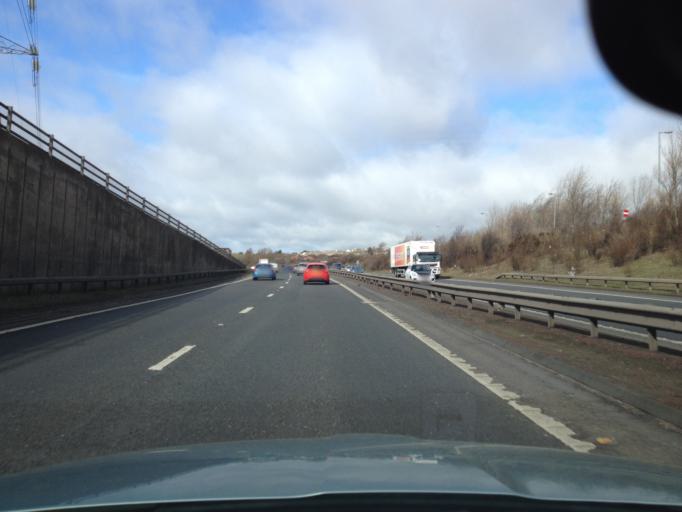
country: GB
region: Scotland
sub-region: Midlothian
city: Loanhead
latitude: 55.8958
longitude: -3.2031
